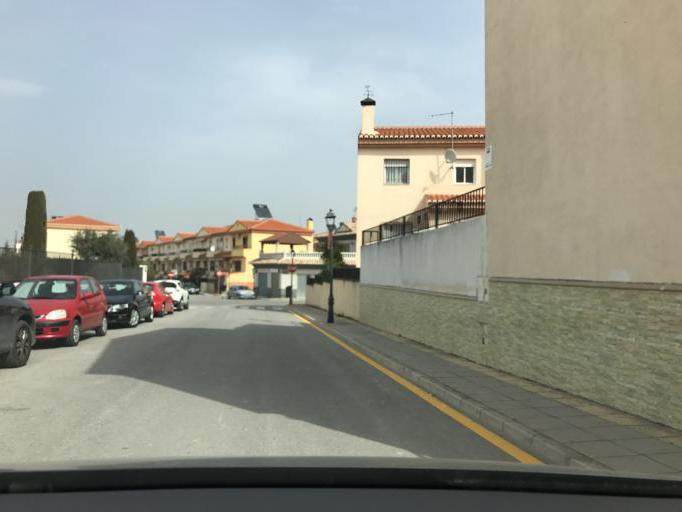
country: ES
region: Andalusia
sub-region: Provincia de Granada
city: Cullar-Vega
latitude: 37.1729
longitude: -3.6949
